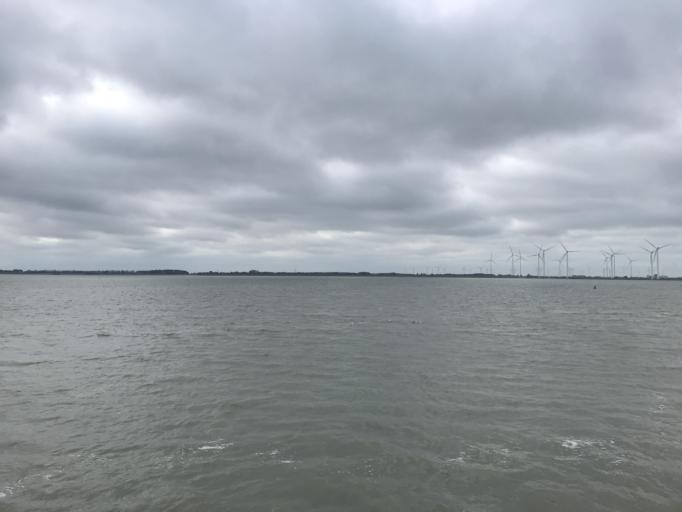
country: NL
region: Groningen
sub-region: Gemeente Delfzijl
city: Delfzijl
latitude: 53.3252
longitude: 7.0357
